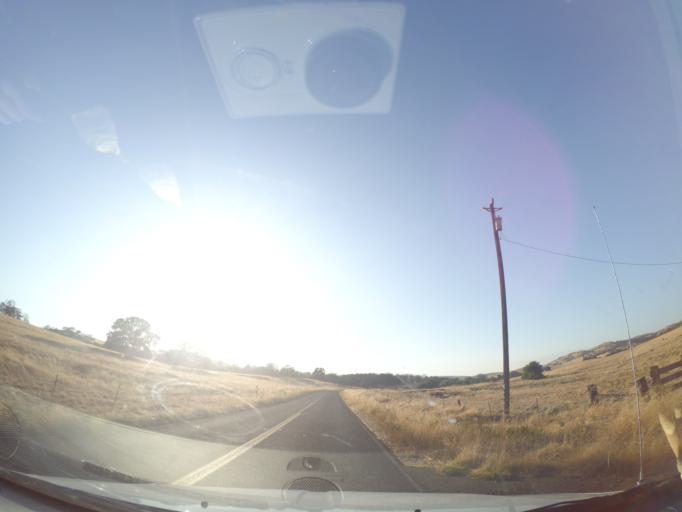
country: US
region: California
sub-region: Merced County
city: Planada
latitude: 37.4895
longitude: -120.2190
